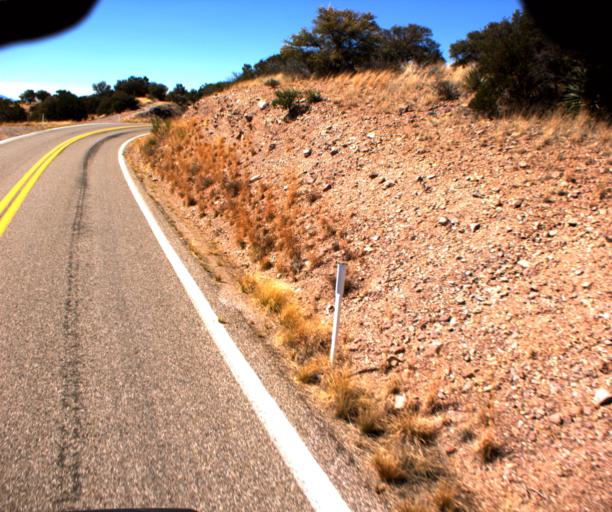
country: US
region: Arizona
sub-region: Cochise County
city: Sierra Vista
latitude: 31.4793
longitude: -110.4812
